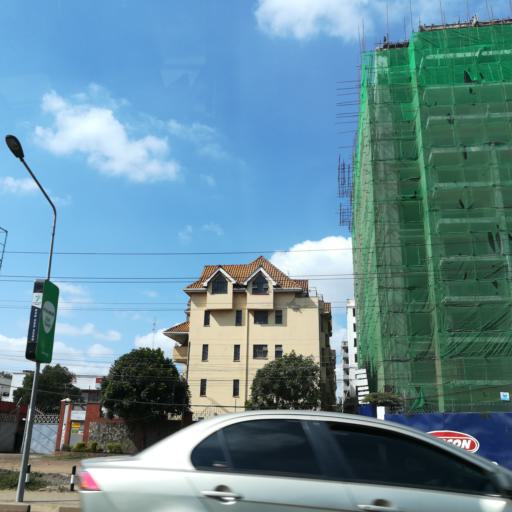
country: KE
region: Nairobi Area
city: Nairobi
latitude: -1.2994
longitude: 36.7946
